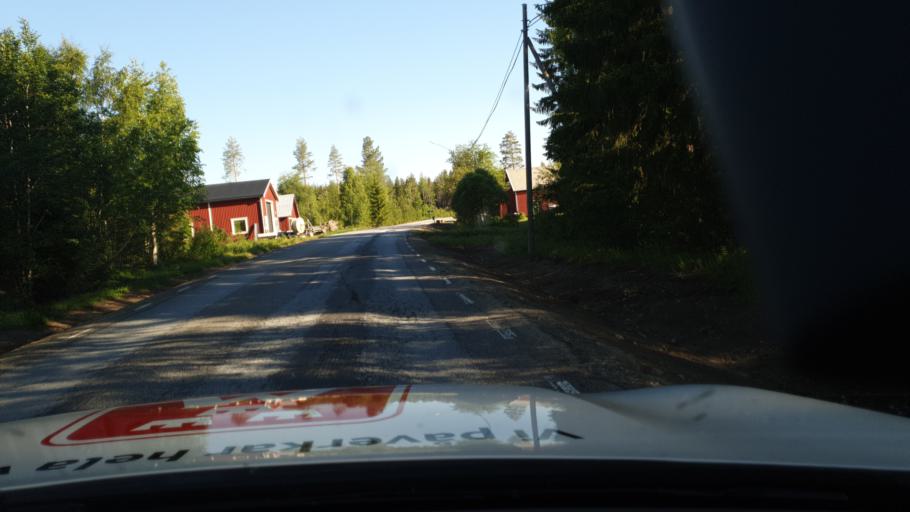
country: SE
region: Vaesterbotten
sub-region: Vannas Kommun
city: Vannasby
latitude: 64.0488
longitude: 20.0674
